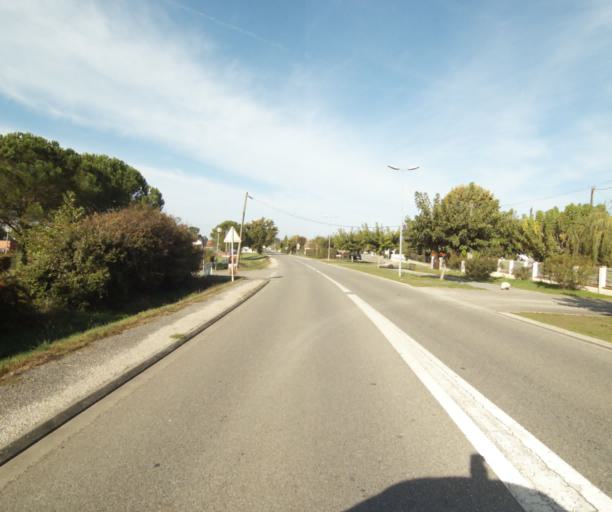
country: FR
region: Midi-Pyrenees
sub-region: Departement du Tarn-et-Garonne
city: Nohic
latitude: 43.9083
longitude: 1.4492
